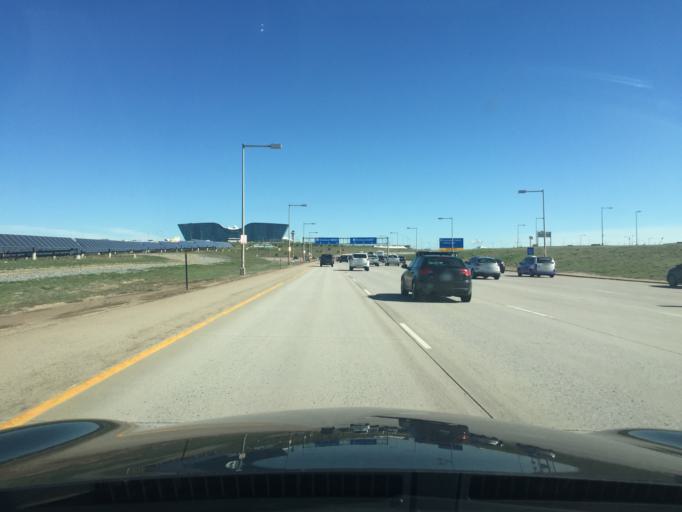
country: US
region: Colorado
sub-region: Weld County
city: Lochbuie
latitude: 39.8382
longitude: -104.6720
